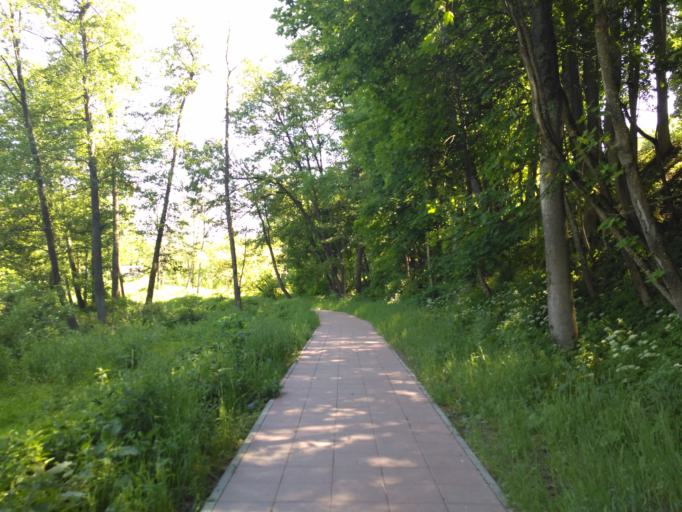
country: BY
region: Minsk
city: Lahoysk
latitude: 54.2036
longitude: 27.8482
